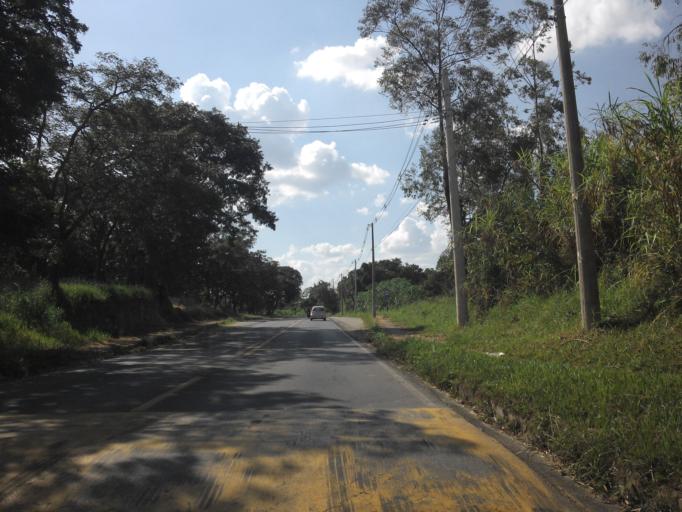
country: BR
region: Sao Paulo
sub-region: Valinhos
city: Valinhos
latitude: -23.0001
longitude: -47.0029
